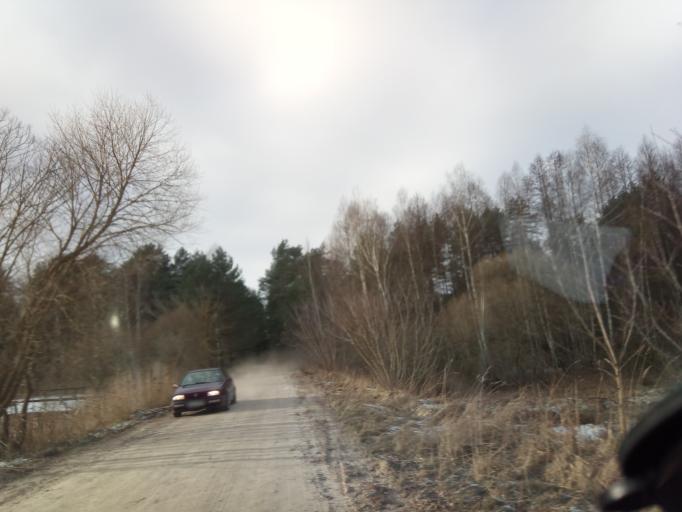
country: LT
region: Alytaus apskritis
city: Varena
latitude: 53.9976
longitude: 24.3532
